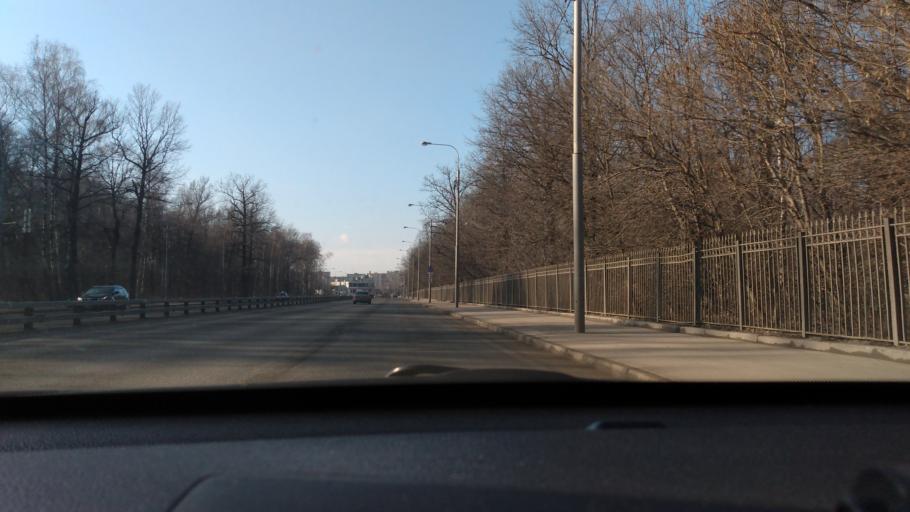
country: RU
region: Moscow
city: Vagonoremont
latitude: 55.8990
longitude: 37.5616
